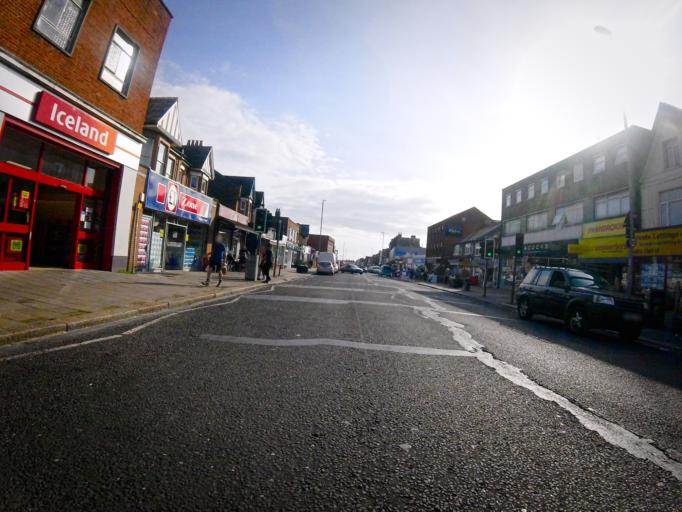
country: GB
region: England
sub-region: East Sussex
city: Portslade
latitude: 50.8345
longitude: -0.2065
